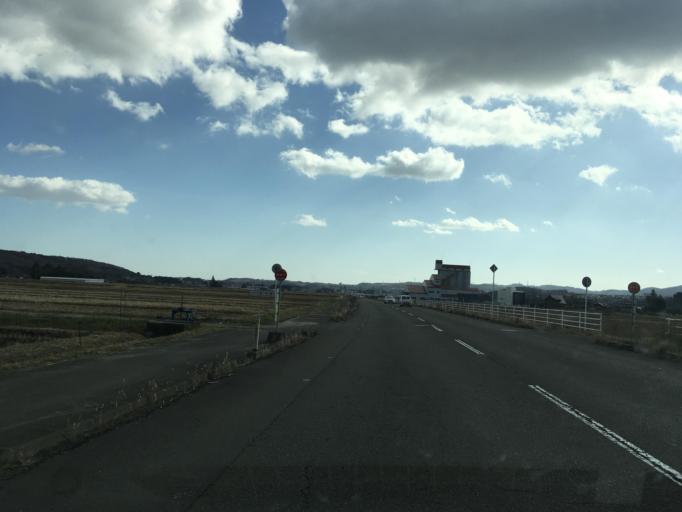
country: JP
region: Miyagi
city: Tomiya
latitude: 38.3502
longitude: 140.7811
